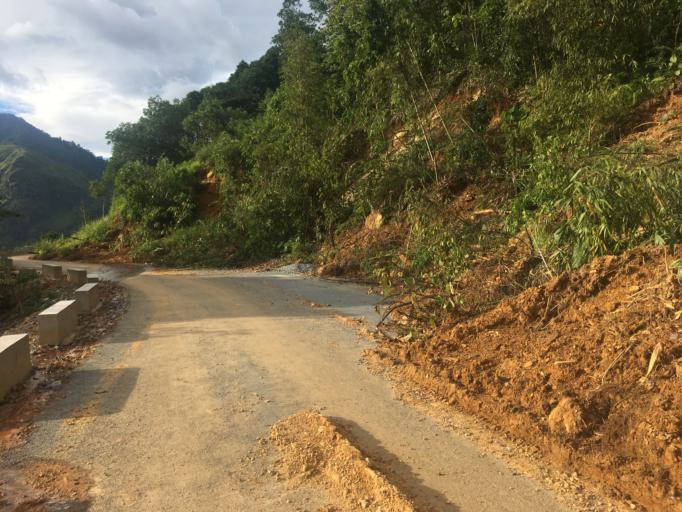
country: VN
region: Ha Giang
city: Thi Tran Tam Son
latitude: 22.9483
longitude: 105.0257
